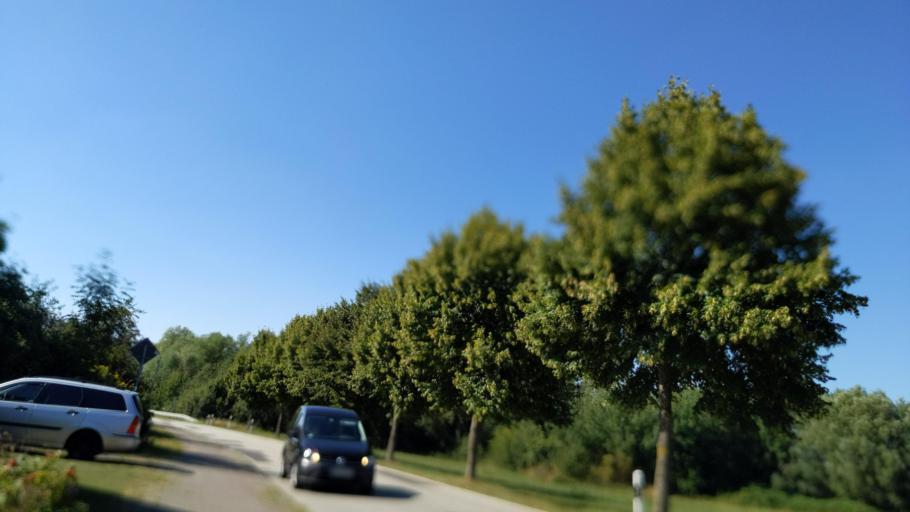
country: DE
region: Mecklenburg-Vorpommern
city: Selmsdorf
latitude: 53.8285
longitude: 10.8842
